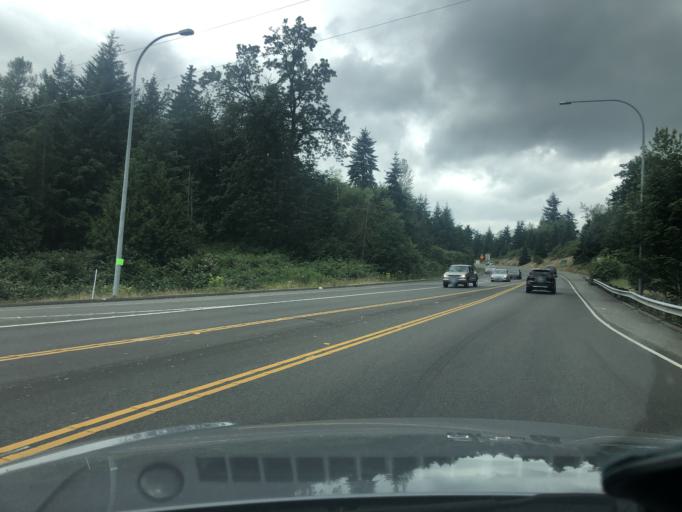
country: US
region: Washington
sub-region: King County
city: Lea Hill
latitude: 47.3306
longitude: -122.1592
